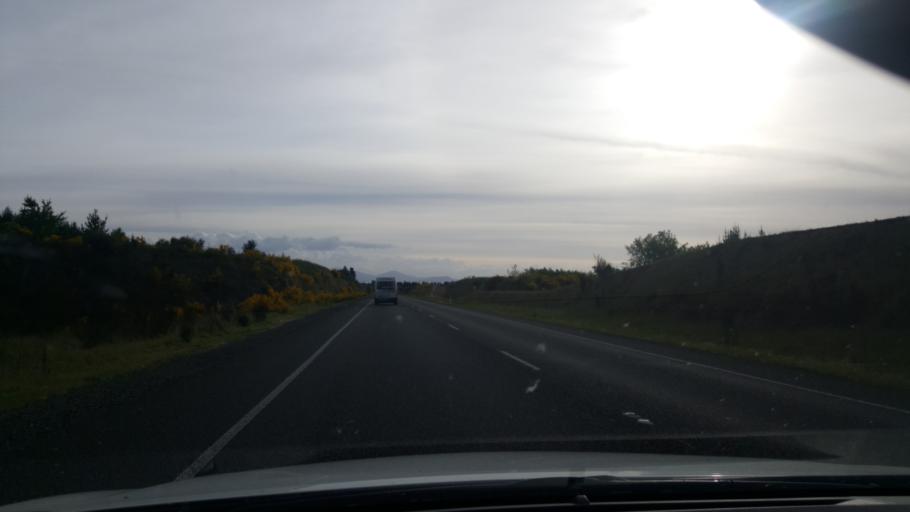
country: NZ
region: Waikato
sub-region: Taupo District
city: Taupo
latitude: -38.7263
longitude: 176.0927
